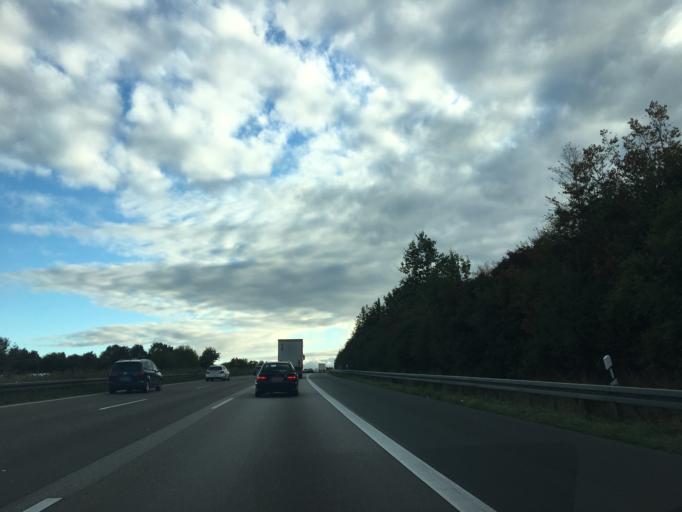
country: DE
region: Hesse
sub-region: Regierungsbezirk Darmstadt
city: Ober-Morlen
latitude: 50.3721
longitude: 8.7052
